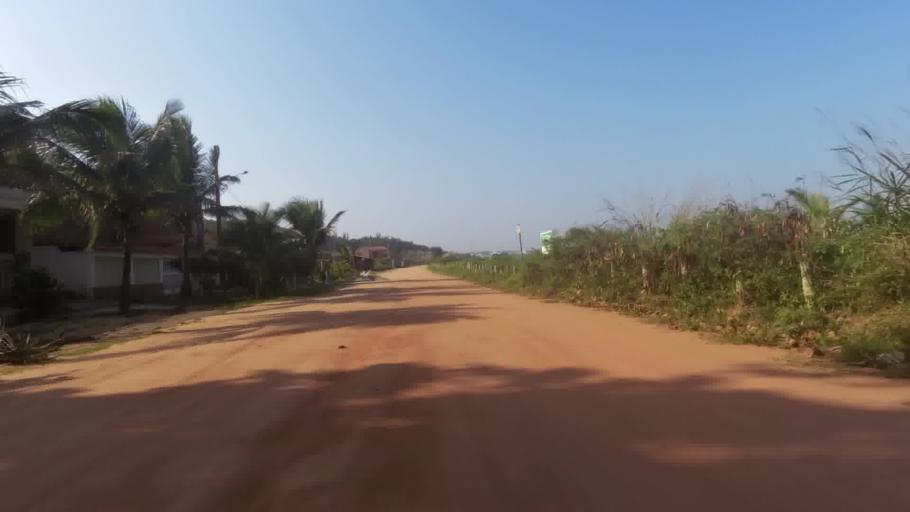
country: BR
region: Espirito Santo
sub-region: Piuma
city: Piuma
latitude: -20.8630
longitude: -40.7580
